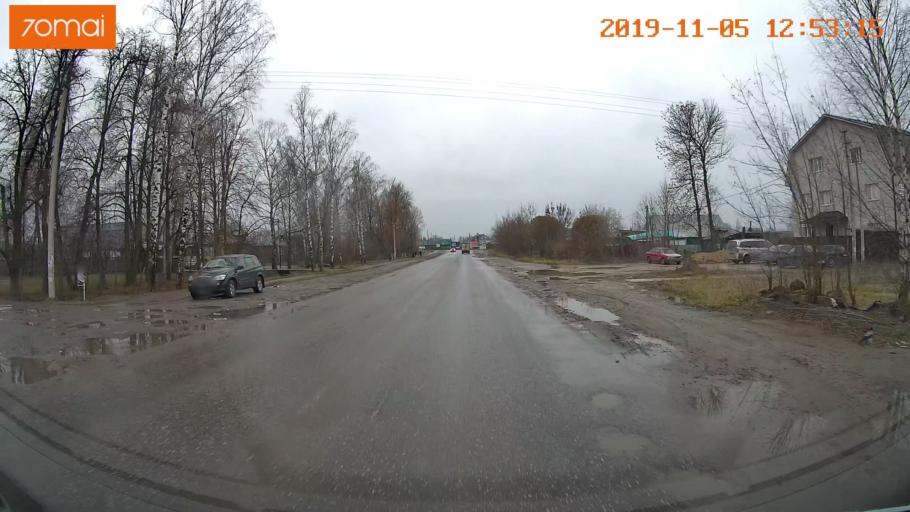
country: RU
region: Ivanovo
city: Kokhma
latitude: 56.9370
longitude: 41.0998
